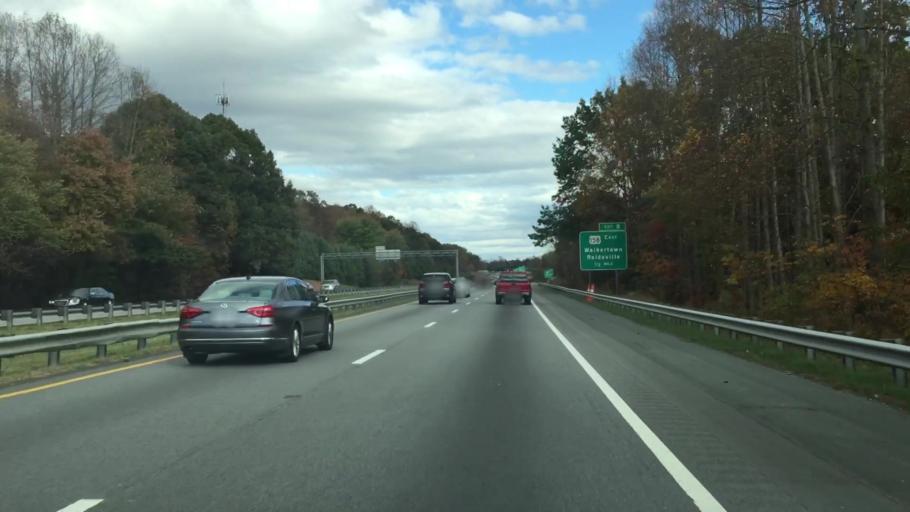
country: US
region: North Carolina
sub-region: Forsyth County
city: Winston-Salem
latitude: 36.0979
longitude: -80.2072
